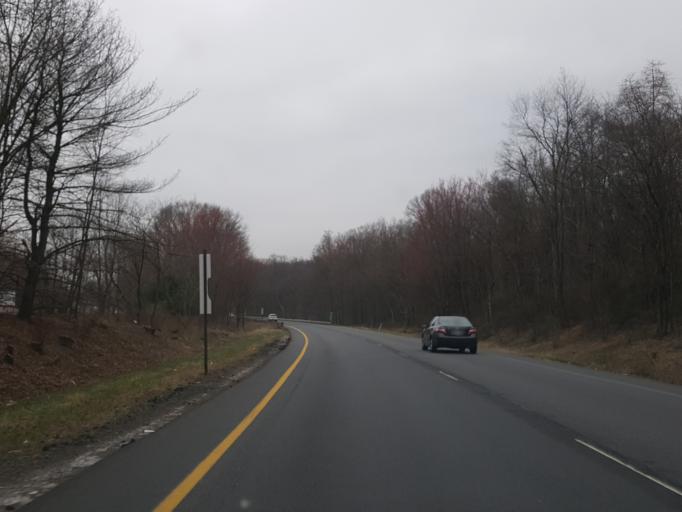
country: US
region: Pennsylvania
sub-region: Schuylkill County
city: Pine Grove
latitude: 40.5684
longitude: -76.4252
